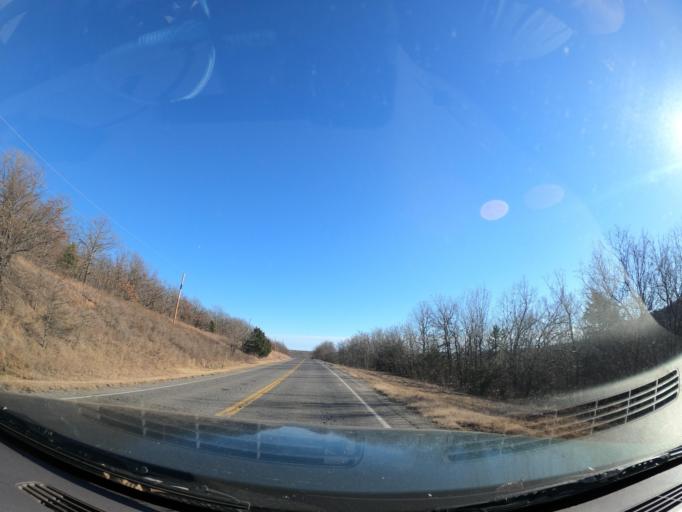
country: US
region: Oklahoma
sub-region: Pittsburg County
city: Longtown
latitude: 35.2189
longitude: -95.4268
